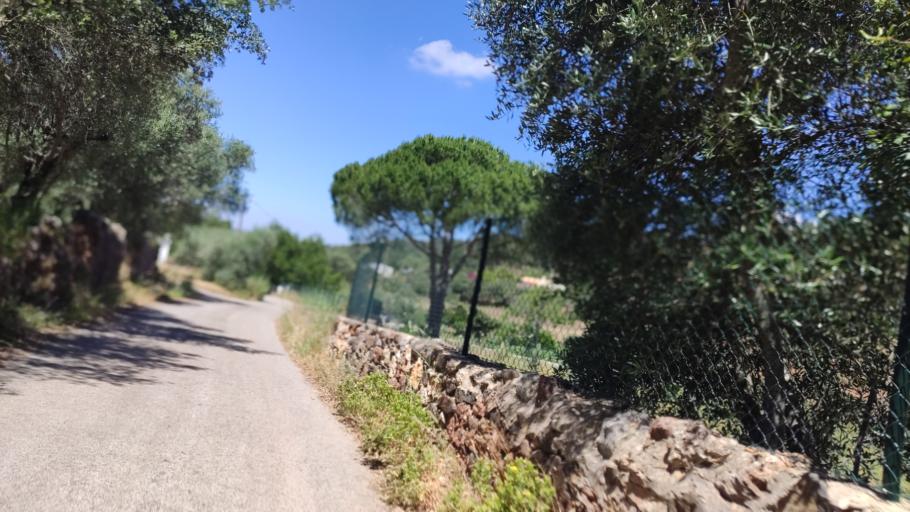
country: PT
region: Faro
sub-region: Sao Bras de Alportel
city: Sao Bras de Alportel
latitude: 37.1736
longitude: -7.9175
